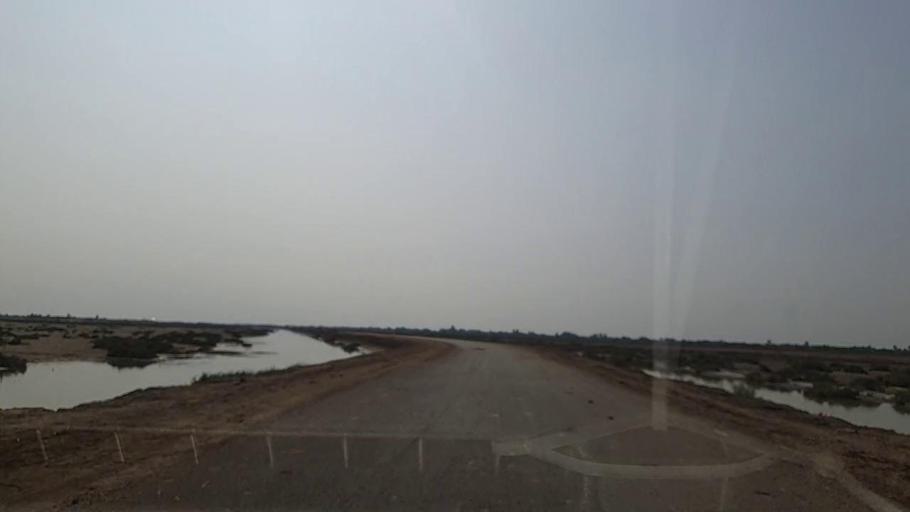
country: PK
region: Sindh
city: Chuhar Jamali
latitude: 24.2048
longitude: 67.8532
